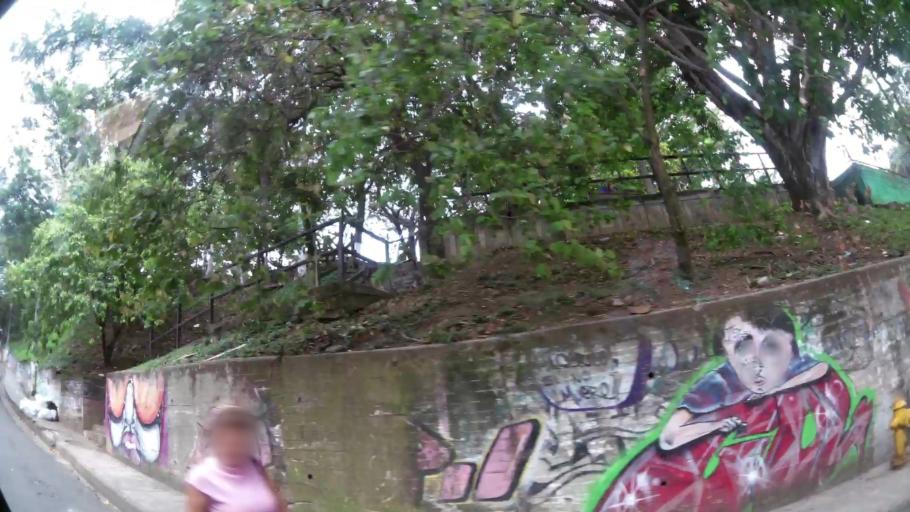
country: CO
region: Antioquia
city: Medellin
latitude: 6.2745
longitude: -75.5603
